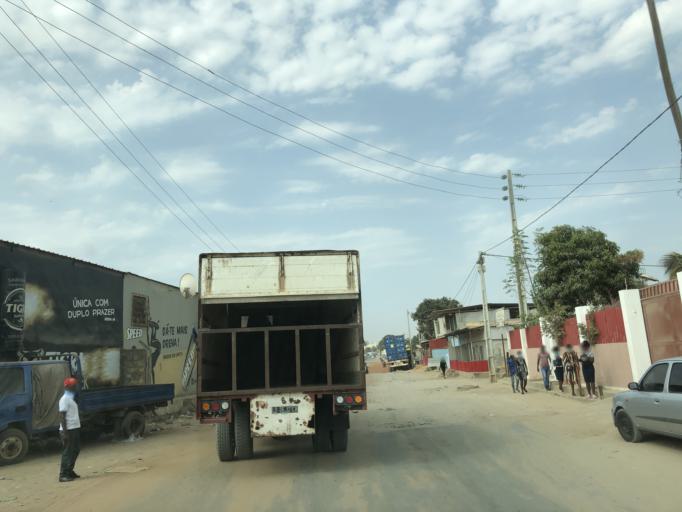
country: AO
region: Luanda
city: Luanda
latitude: -8.8966
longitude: 13.3514
